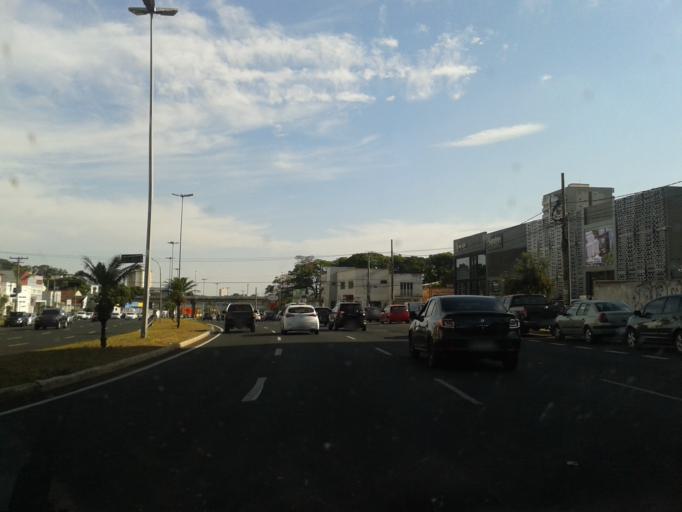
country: BR
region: Minas Gerais
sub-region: Uberlandia
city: Uberlandia
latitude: -18.9227
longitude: -48.2705
